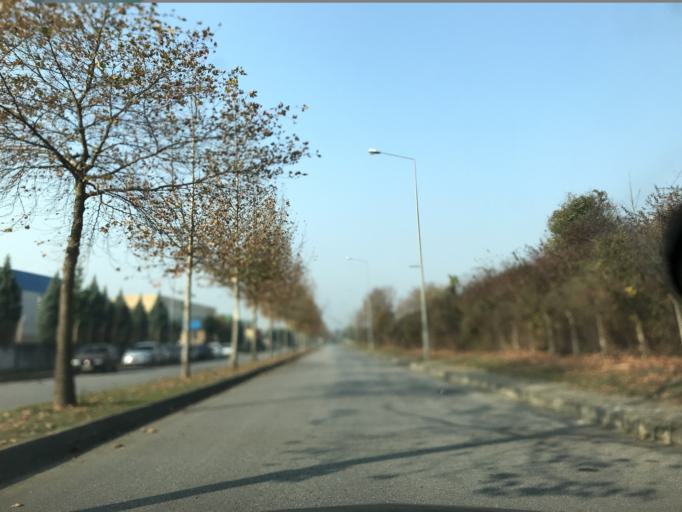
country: TR
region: Duzce
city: Duzce
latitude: 40.7864
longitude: 31.1424
